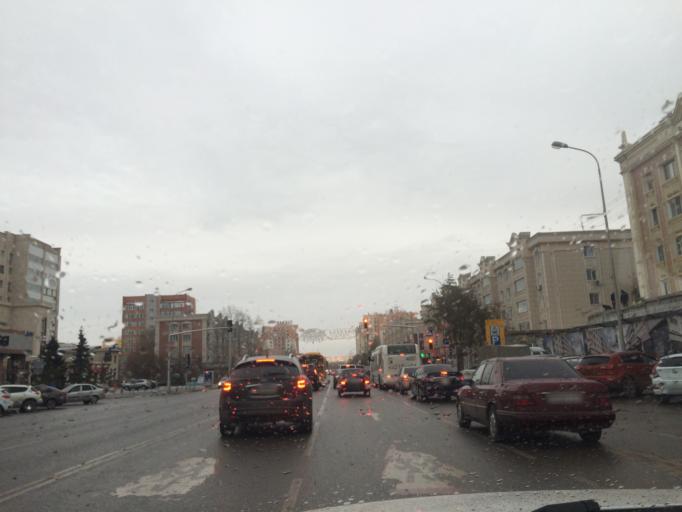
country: KZ
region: Astana Qalasy
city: Astana
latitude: 51.1613
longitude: 71.4284
